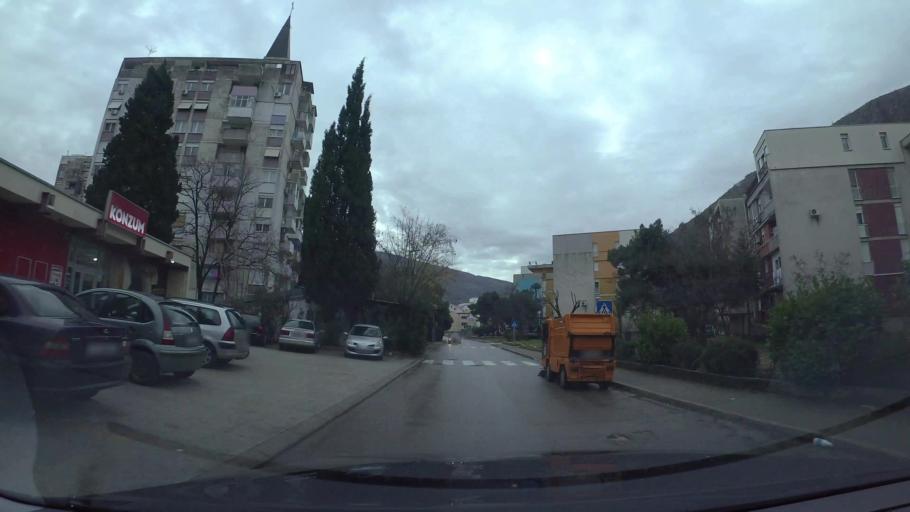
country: BA
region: Federation of Bosnia and Herzegovina
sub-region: Hercegovacko-Bosanski Kanton
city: Mostar
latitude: 43.3377
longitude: 17.8073
